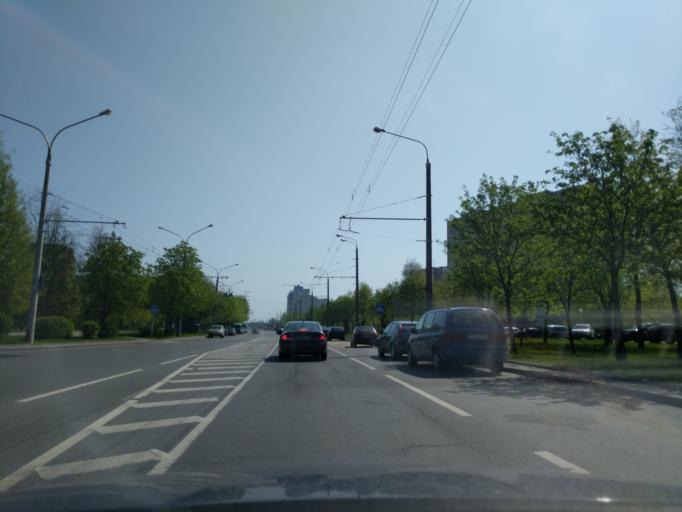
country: BY
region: Minsk
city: Malinovka
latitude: 53.8595
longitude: 27.4659
